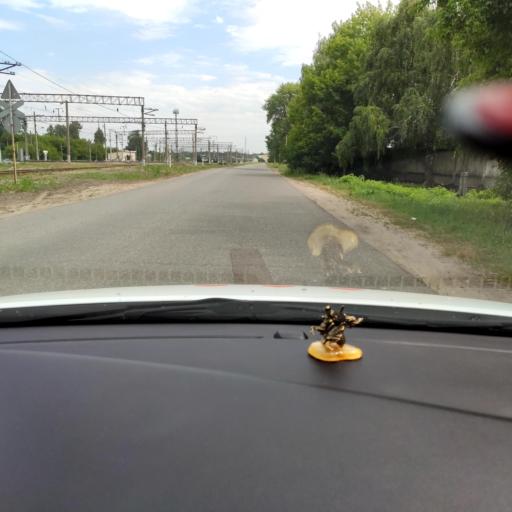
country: RU
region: Tatarstan
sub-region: Zelenodol'skiy Rayon
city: Zelenodolsk
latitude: 55.8411
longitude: 48.5459
